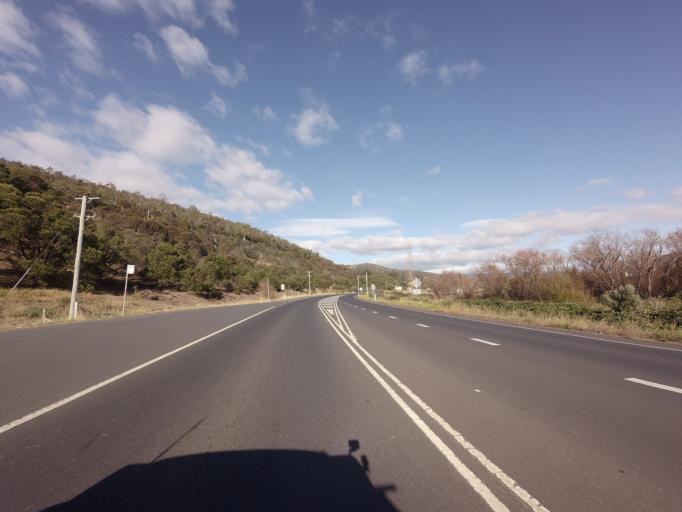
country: AU
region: Tasmania
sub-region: Derwent Valley
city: New Norfolk
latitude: -42.7828
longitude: 147.1073
